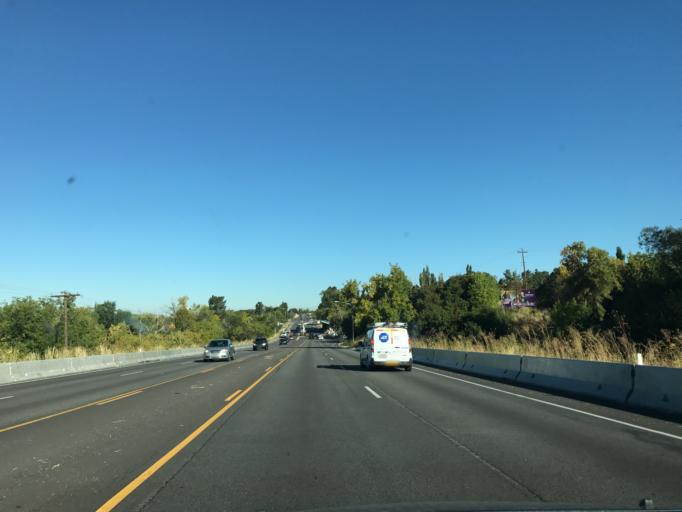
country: US
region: Utah
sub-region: Weber County
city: Uintah
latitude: 41.1662
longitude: -111.9434
